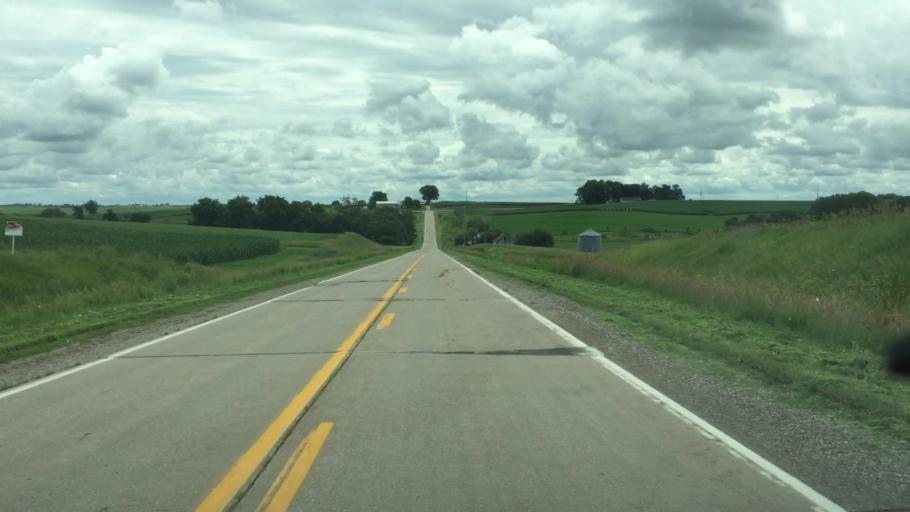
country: US
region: Iowa
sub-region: Jasper County
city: Monroe
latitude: 41.5808
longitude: -93.1084
